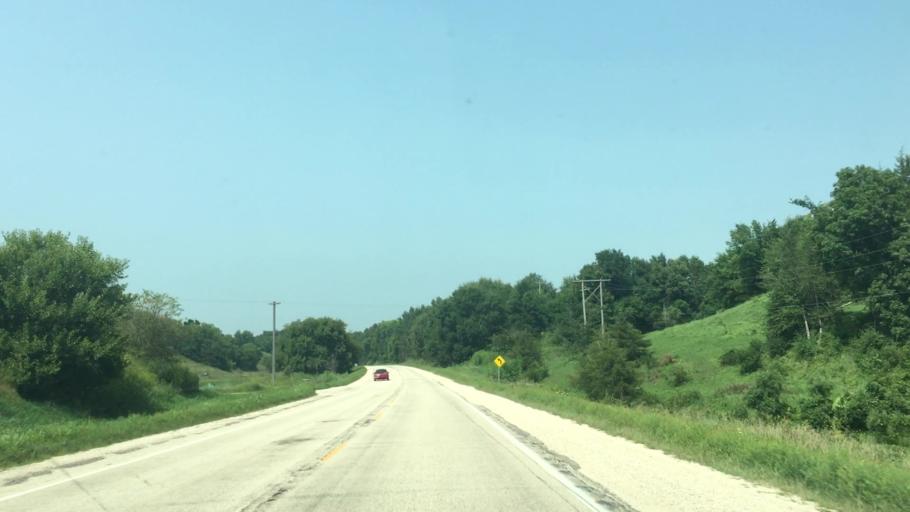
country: US
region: Iowa
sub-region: Fayette County
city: West Union
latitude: 43.0711
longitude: -91.8388
